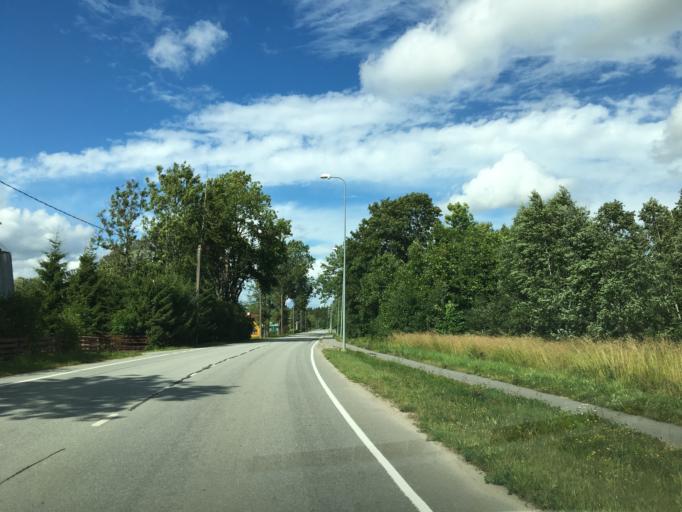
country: EE
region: Paernumaa
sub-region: Vaendra vald (alev)
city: Vandra
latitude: 58.6191
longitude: 25.1035
